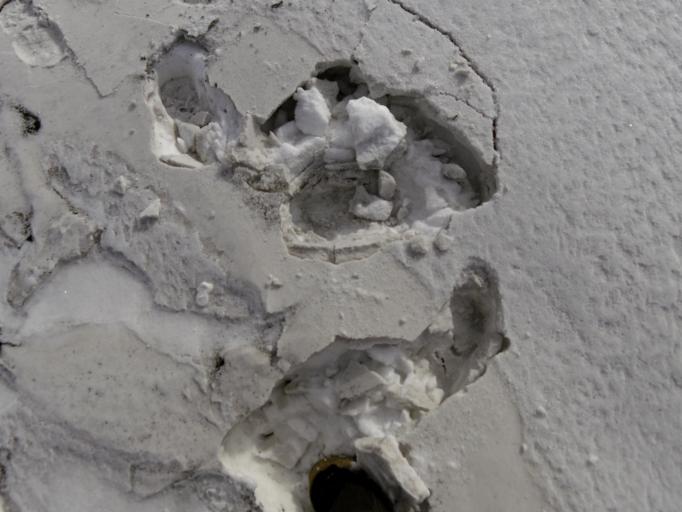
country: US
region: North Dakota
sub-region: Walsh County
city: Grafton
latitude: 48.3977
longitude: -97.2077
